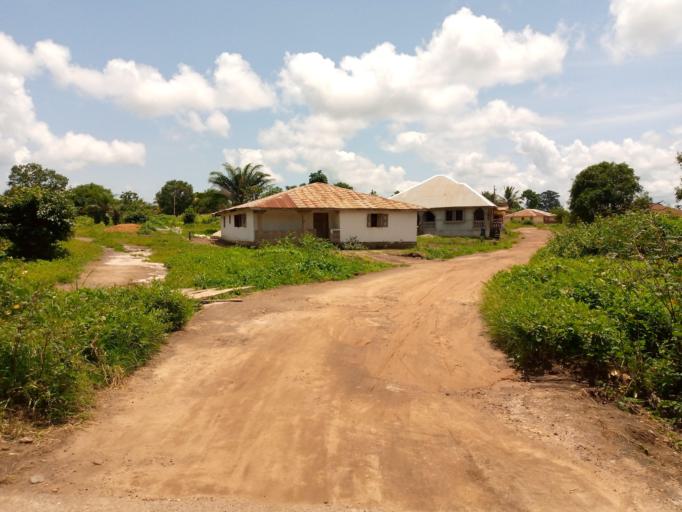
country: SL
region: Northern Province
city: Magburaka
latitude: 8.7167
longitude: -11.9604
